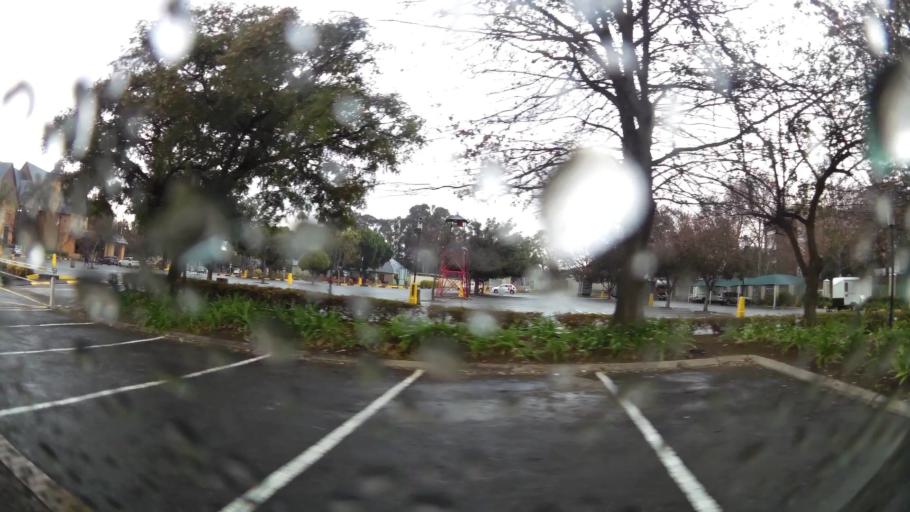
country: ZA
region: Gauteng
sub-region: City of Johannesburg Metropolitan Municipality
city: Johannesburg
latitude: -26.1352
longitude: 28.0526
